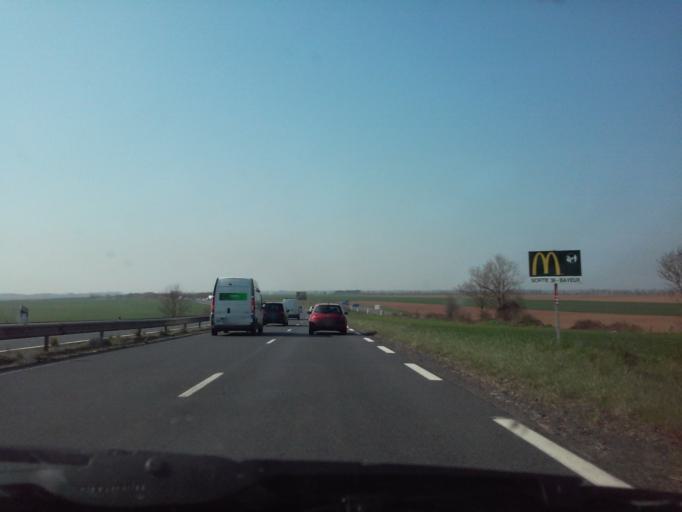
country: FR
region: Lower Normandy
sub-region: Departement du Calvados
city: Tilly-sur-Seulles
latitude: 49.2426
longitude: -0.6069
